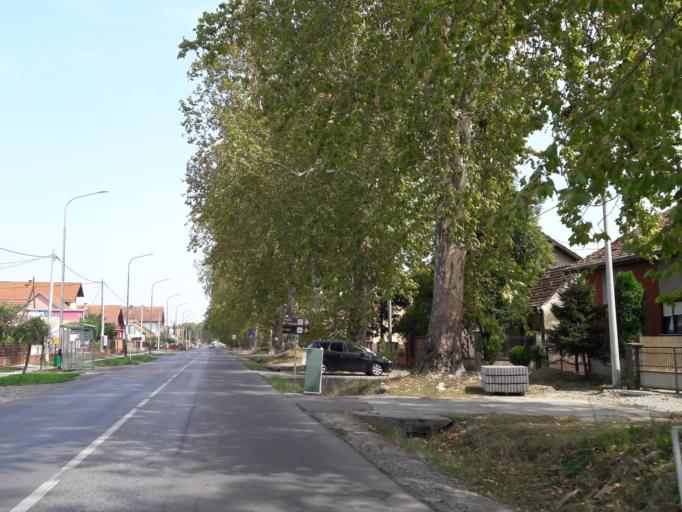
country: HR
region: Osjecko-Baranjska
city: Visnjevac
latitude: 45.5300
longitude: 18.6146
